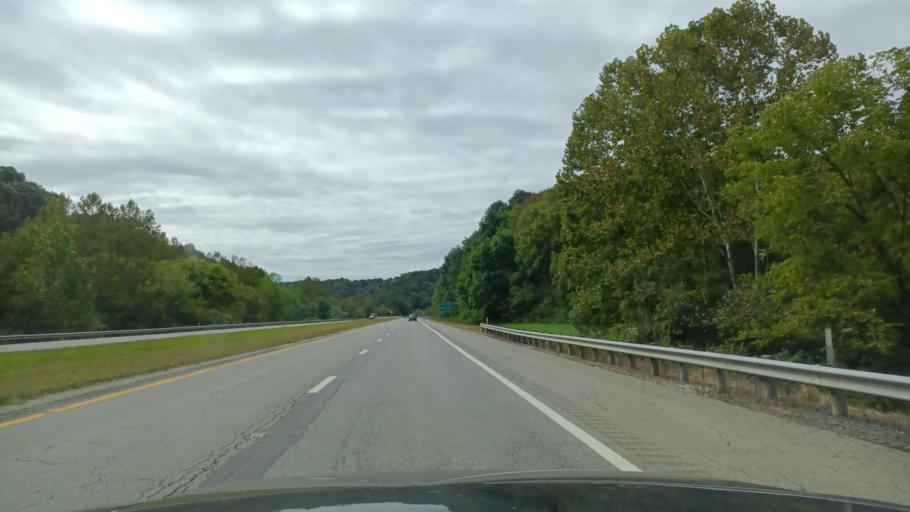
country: US
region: Ohio
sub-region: Washington County
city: Newport
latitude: 39.2398
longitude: -81.2163
